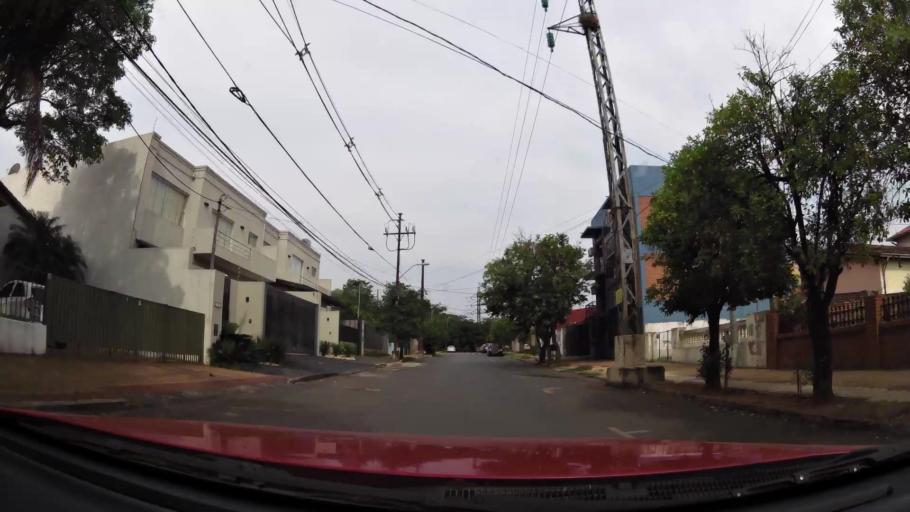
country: PY
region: Central
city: Lambare
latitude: -25.2945
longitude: -57.5699
